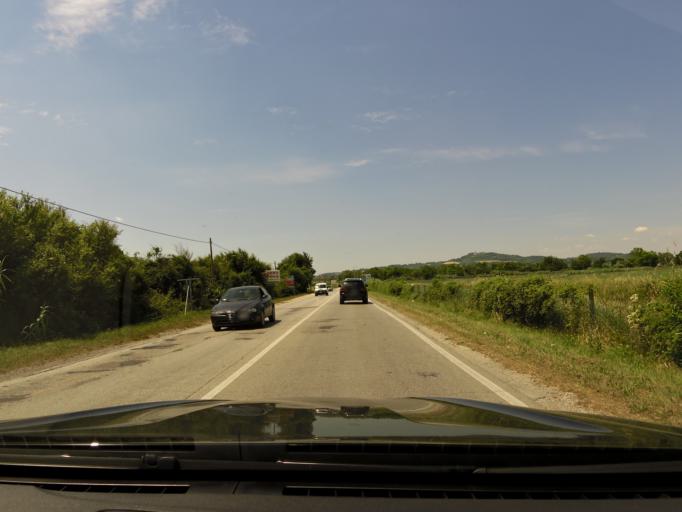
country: IT
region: The Marches
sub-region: Provincia di Pesaro e Urbino
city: Rosciano
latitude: 43.8192
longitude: 13.0214
